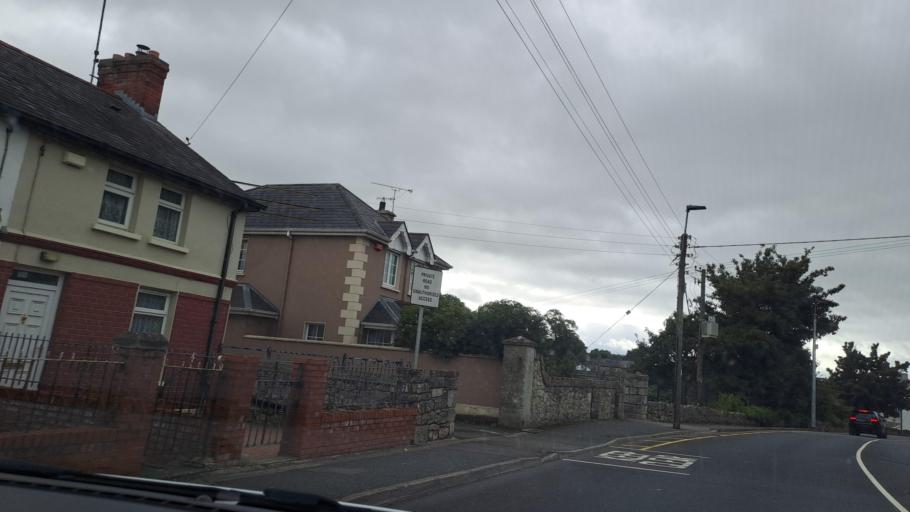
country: IE
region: Ulster
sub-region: County Monaghan
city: Carrickmacross
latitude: 53.9788
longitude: -6.7173
